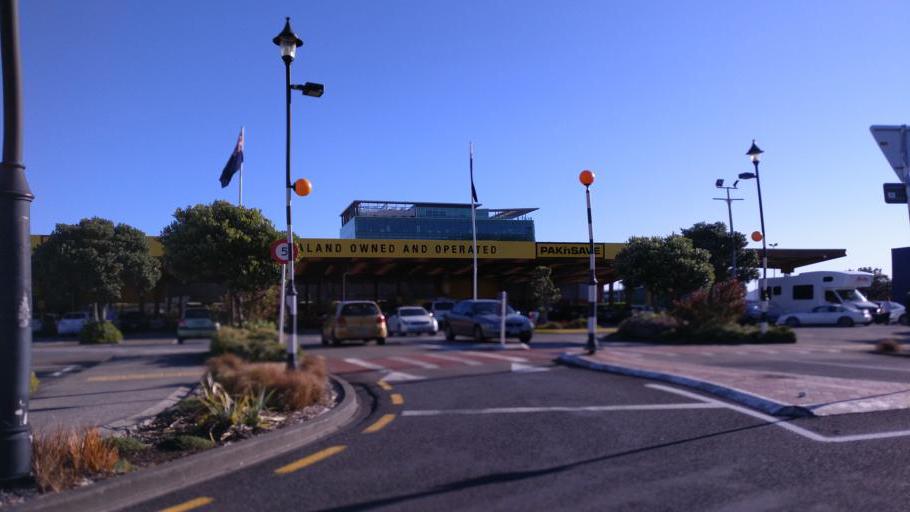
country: NZ
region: Wellington
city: Petone
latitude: -41.2238
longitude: 174.8726
